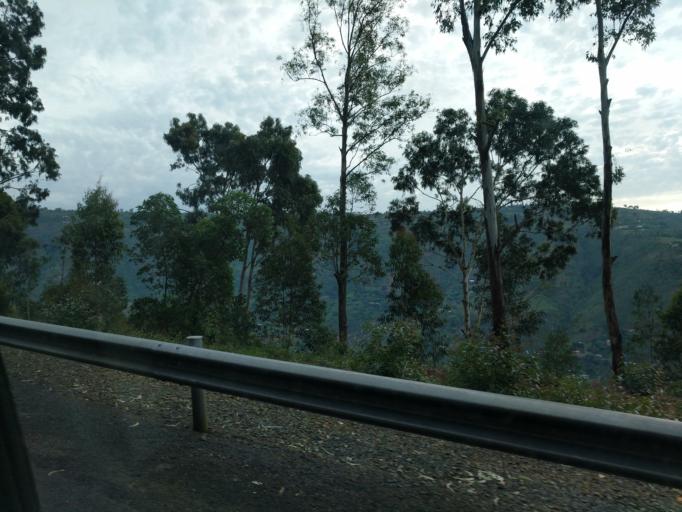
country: RW
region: Kigali
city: Kigali
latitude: -1.9340
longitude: 30.0262
